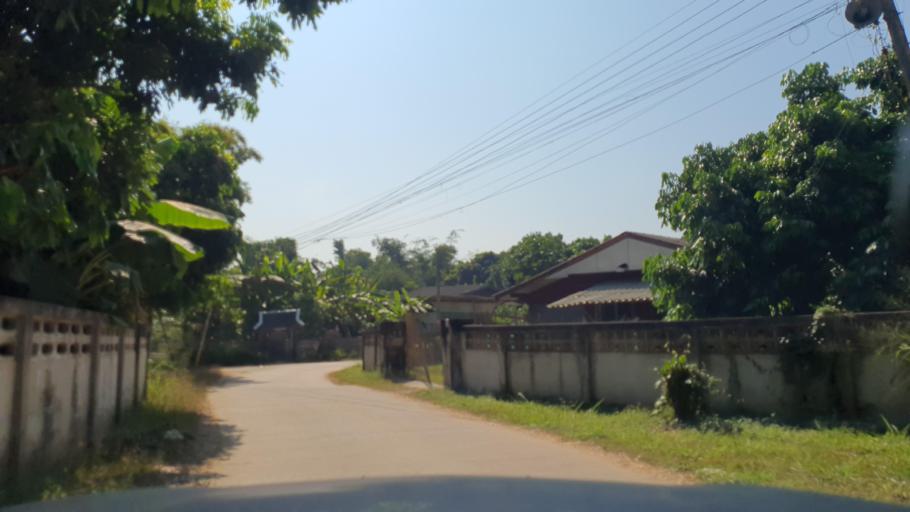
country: TH
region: Lamphun
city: Mae Tha
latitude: 18.5460
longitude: 99.2458
